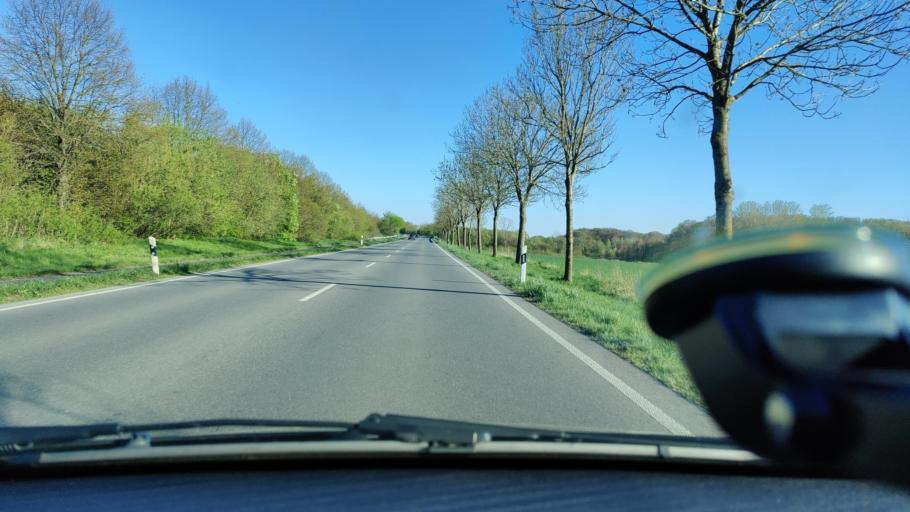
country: DE
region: North Rhine-Westphalia
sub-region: Regierungsbezirk Munster
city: Coesfeld
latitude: 51.9208
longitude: 7.1629
